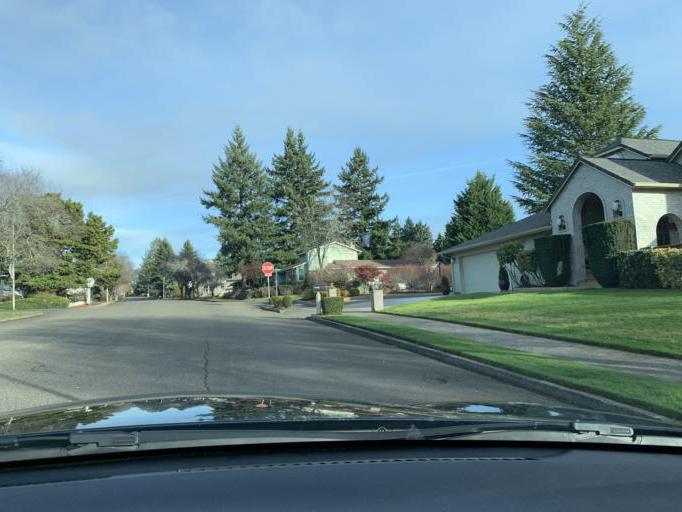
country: US
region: Washington
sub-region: Clark County
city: Mill Plain
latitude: 45.5996
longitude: -122.5181
